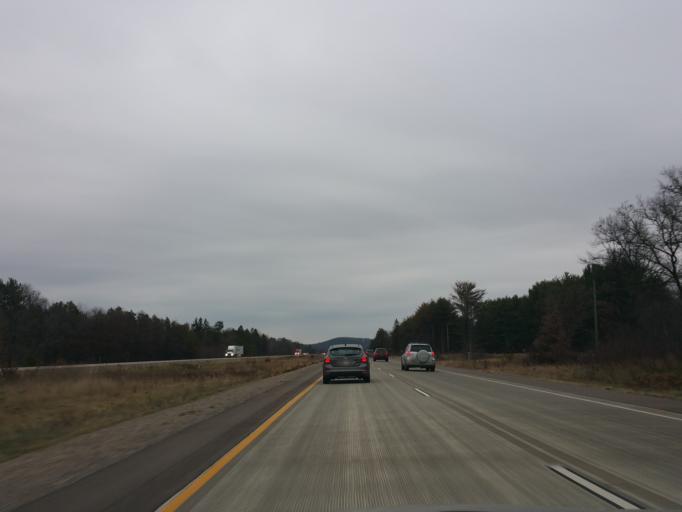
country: US
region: Wisconsin
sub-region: Jackson County
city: Black River Falls
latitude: 44.3523
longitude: -90.9453
